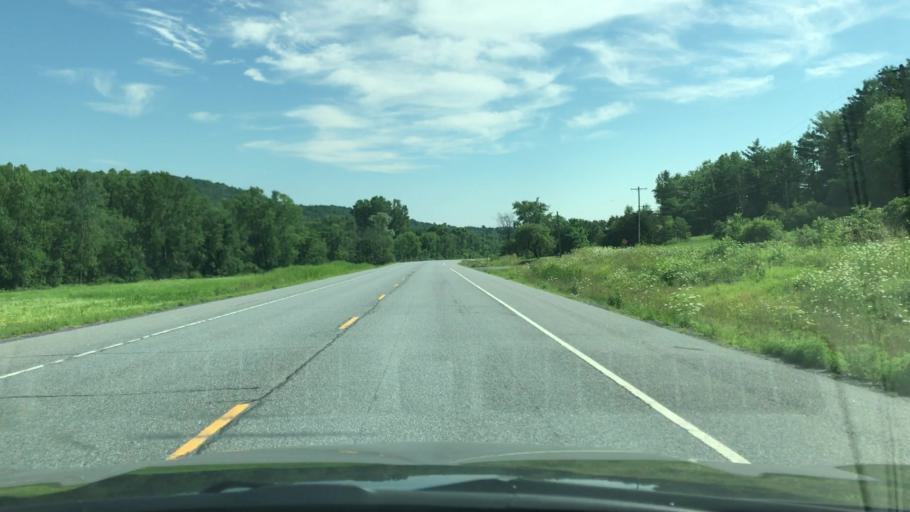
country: US
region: New York
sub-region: Washington County
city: Whitehall
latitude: 43.4781
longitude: -73.4313
